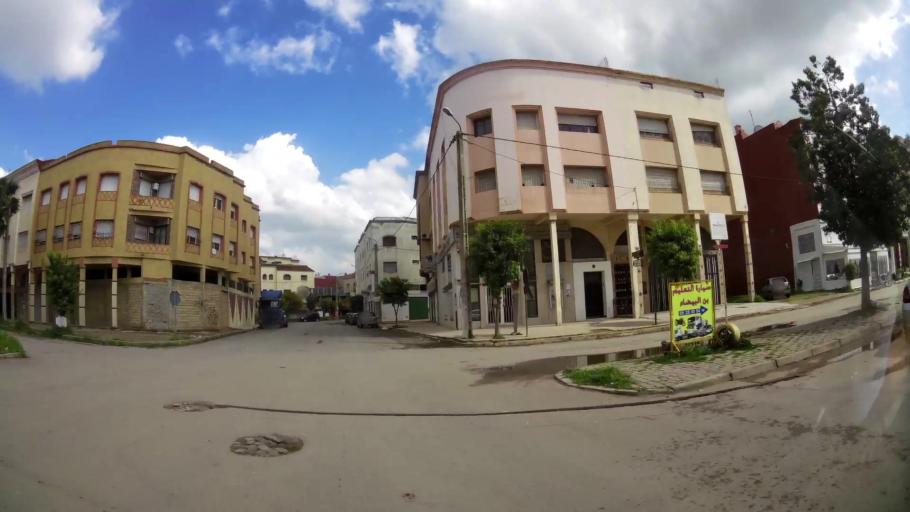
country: MA
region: Grand Casablanca
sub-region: Mediouna
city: Mediouna
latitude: 33.3763
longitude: -7.5355
